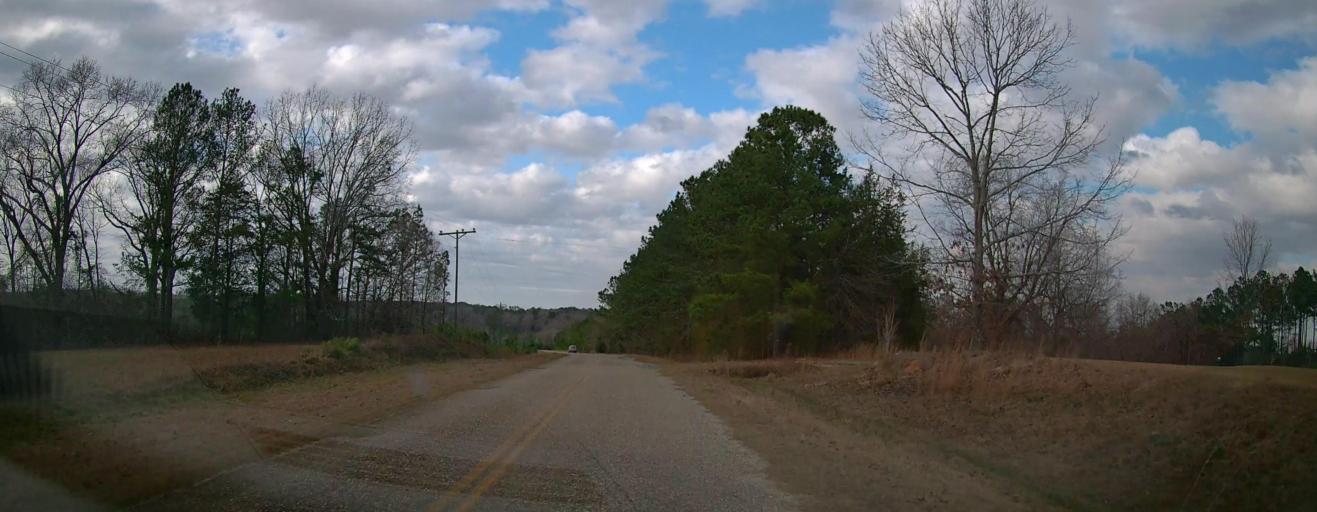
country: US
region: Georgia
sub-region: Marion County
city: Buena Vista
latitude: 32.4228
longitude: -84.4167
